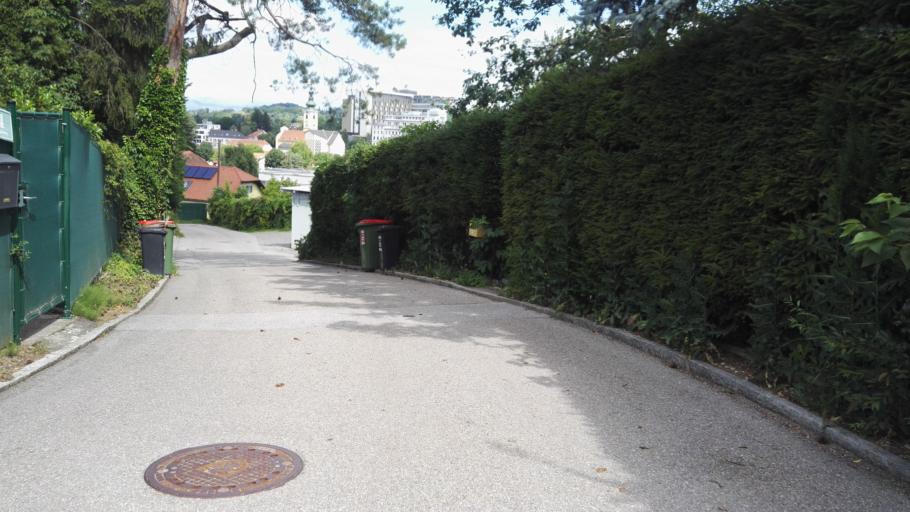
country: AT
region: Styria
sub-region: Graz Stadt
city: Graz
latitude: 47.0759
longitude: 15.4701
